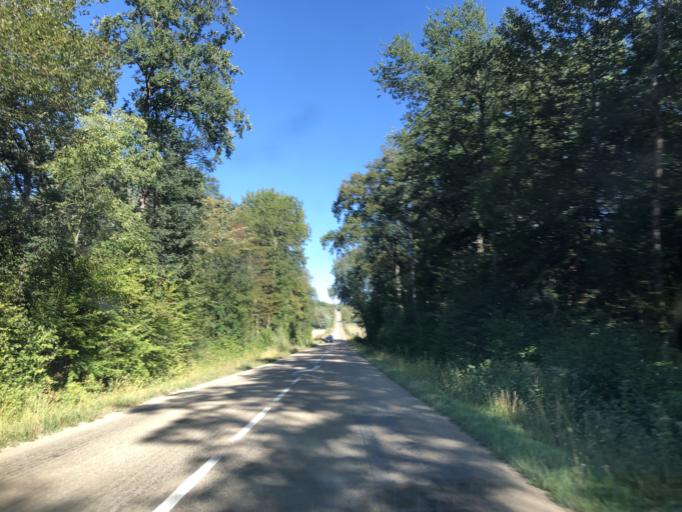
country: FR
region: Bourgogne
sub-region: Departement de l'Yonne
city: Seignelay
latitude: 47.8998
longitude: 3.5770
